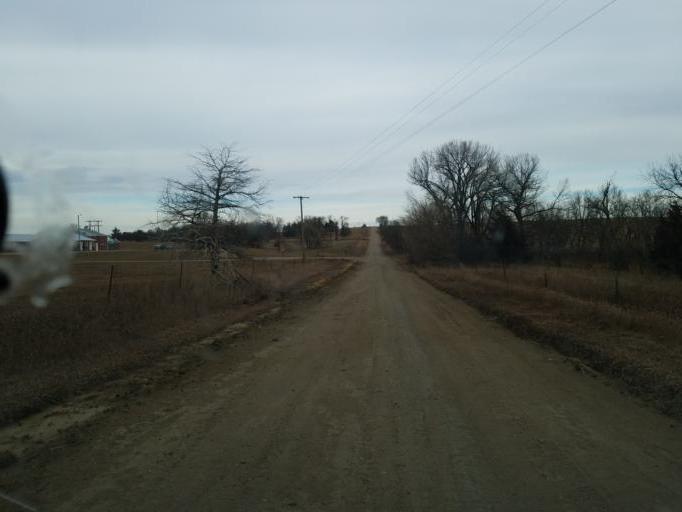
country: US
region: Nebraska
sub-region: Knox County
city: Bloomfield
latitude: 42.5687
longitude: -97.7206
